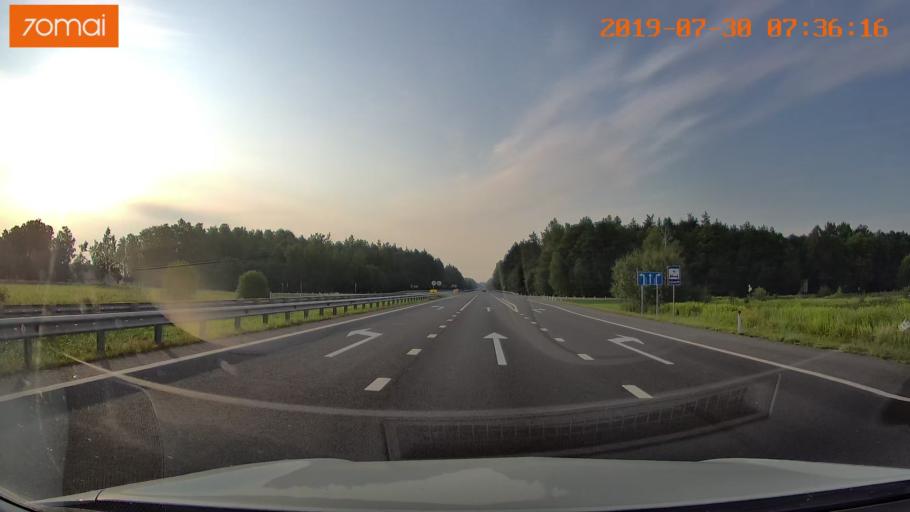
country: RU
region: Kaliningrad
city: Gvardeysk
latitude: 54.6660
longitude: 21.1206
